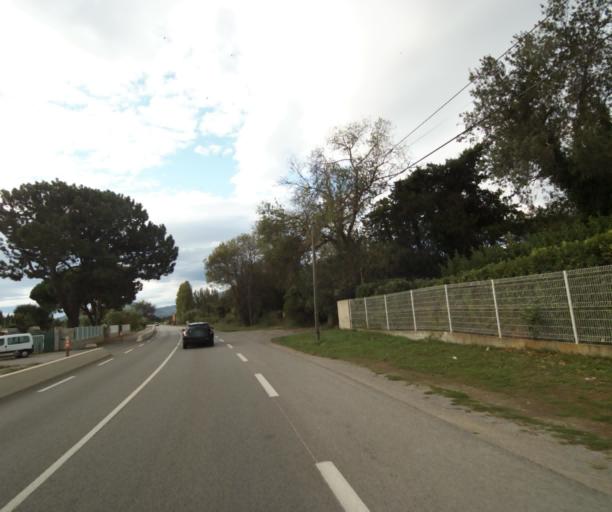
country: FR
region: Languedoc-Roussillon
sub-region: Departement des Pyrenees-Orientales
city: Argelers
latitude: 42.5799
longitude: 3.0327
